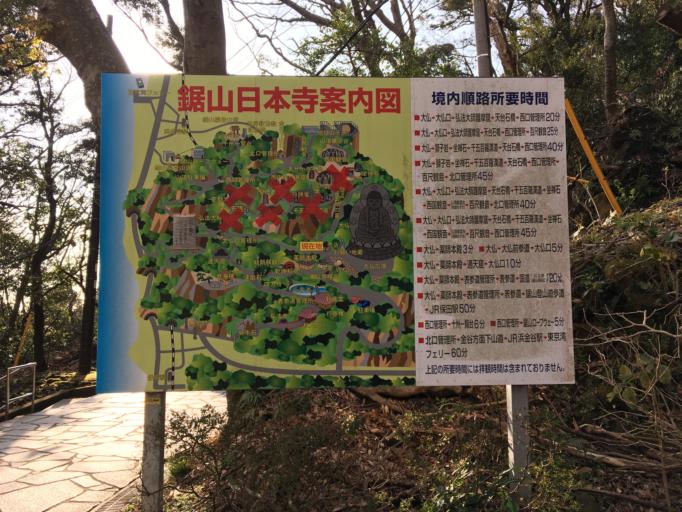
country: JP
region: Chiba
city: Futtsu
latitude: 35.1575
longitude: 139.8339
